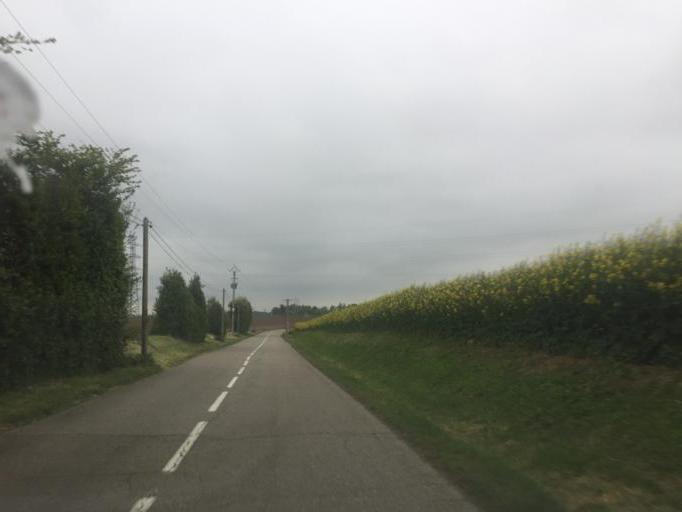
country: FR
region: Rhone-Alpes
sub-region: Departement de l'Ain
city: Beynost
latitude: 45.8516
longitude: 4.9951
